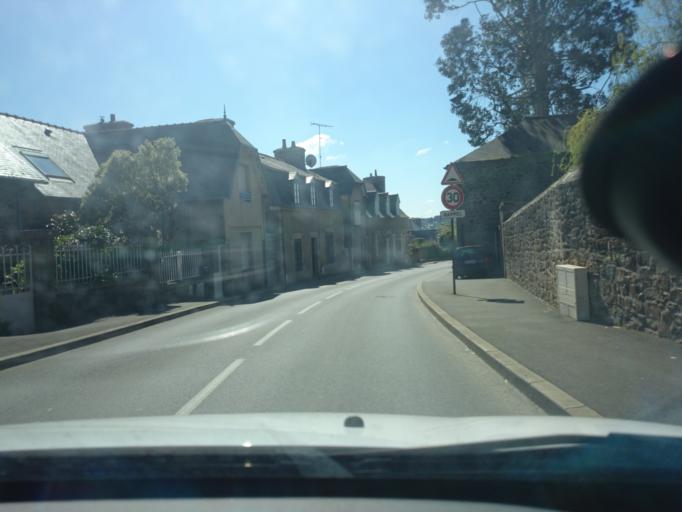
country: FR
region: Brittany
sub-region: Departement des Cotes-d'Armor
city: Perros-Guirec
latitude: 48.8119
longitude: -3.4390
